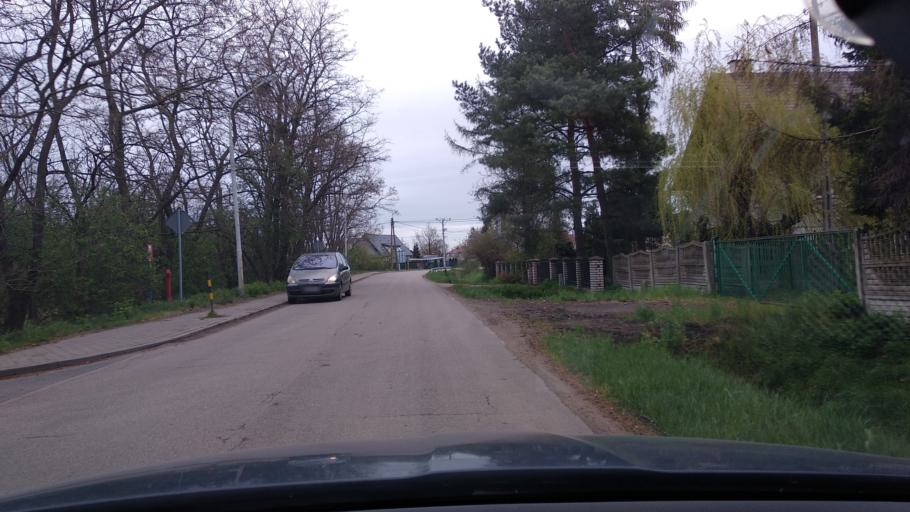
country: PL
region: Pomeranian Voivodeship
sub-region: Powiat gdanski
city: Pruszcz Gdanski
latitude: 54.2754
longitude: 18.6787
